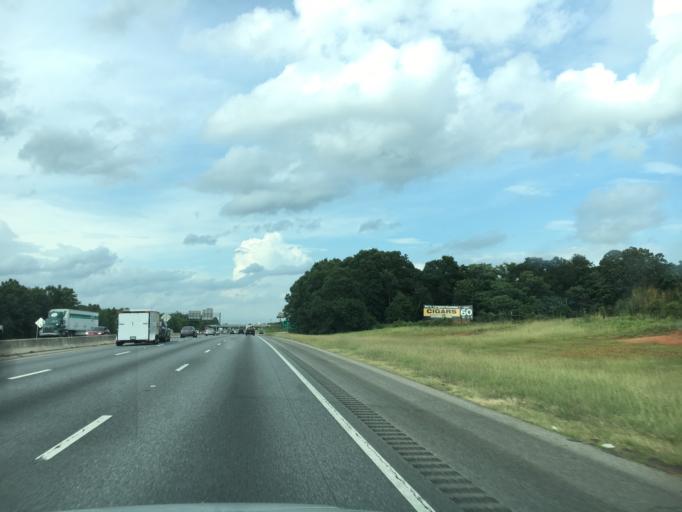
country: US
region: South Carolina
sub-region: Anderson County
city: Piedmont
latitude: 34.7031
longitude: -82.5012
